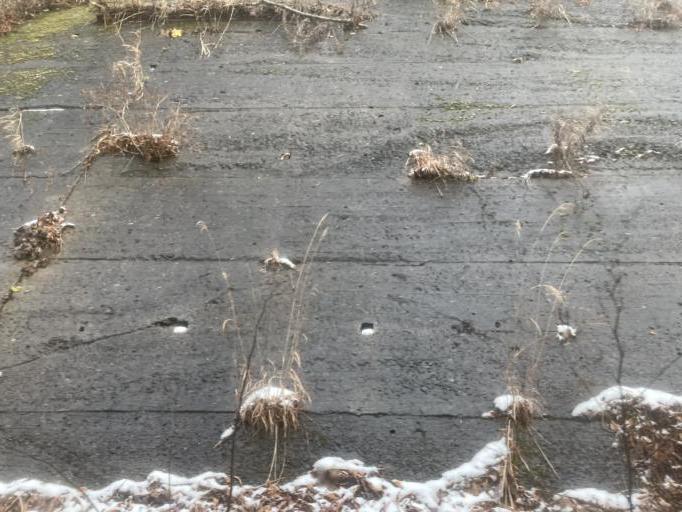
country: JP
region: Aomori
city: Goshogawara
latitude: 41.0995
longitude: 140.5282
